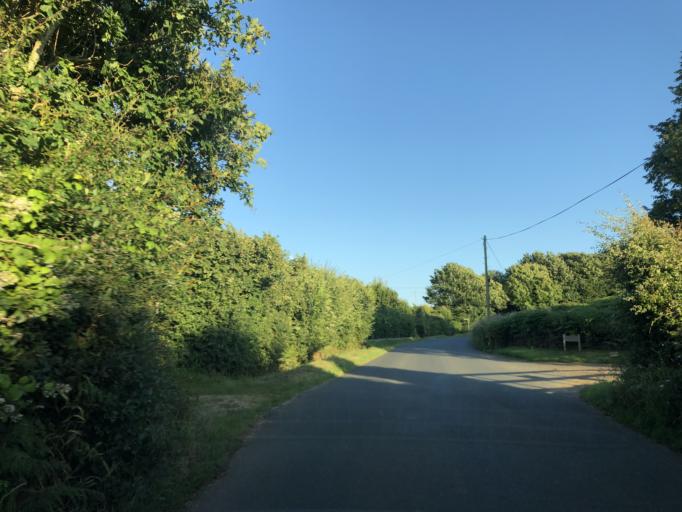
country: GB
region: England
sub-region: Isle of Wight
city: Chale
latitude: 50.6310
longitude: -1.3239
